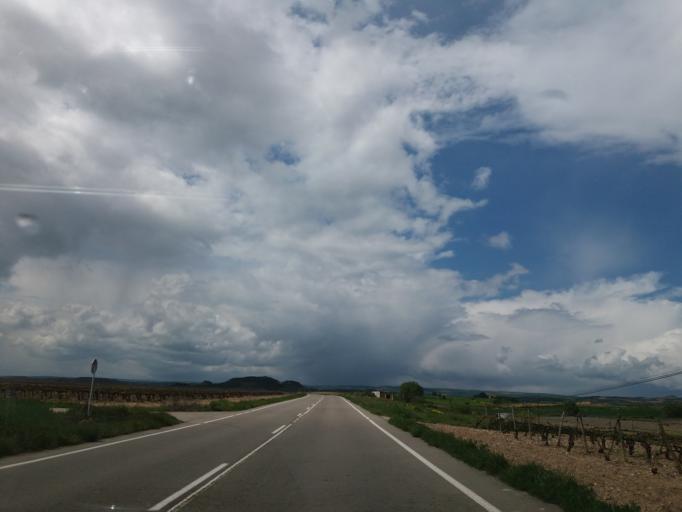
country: ES
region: La Rioja
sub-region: Provincia de La Rioja
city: Sajazarra
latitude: 42.5738
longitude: -2.9455
